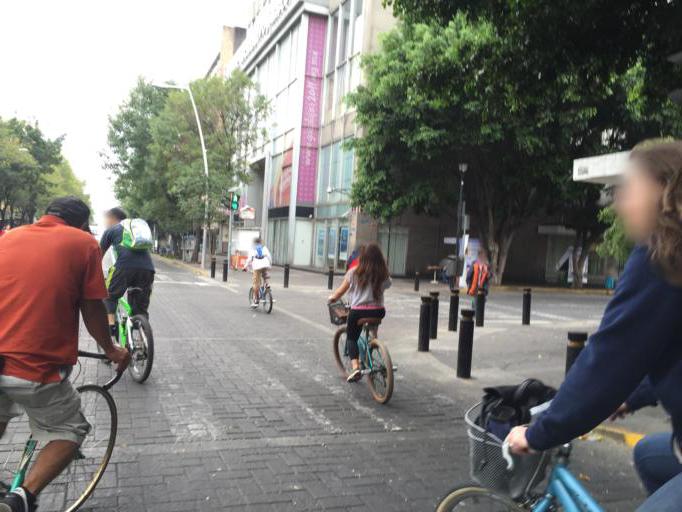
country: MX
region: Jalisco
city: Guadalajara
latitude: 20.6752
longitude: -103.3466
